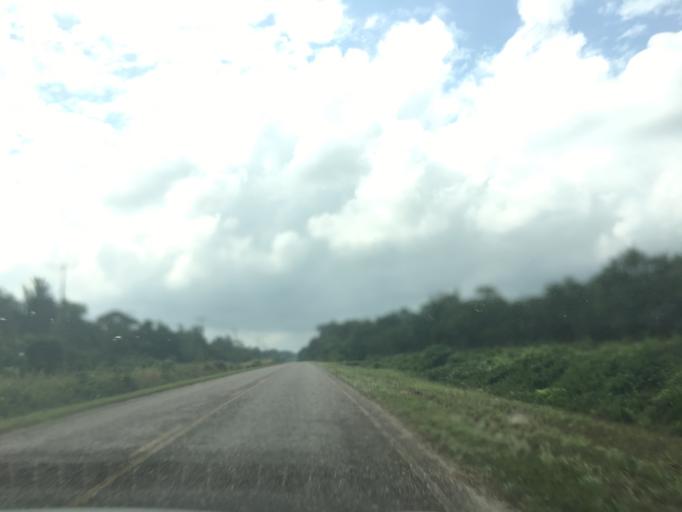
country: BZ
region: Stann Creek
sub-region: Dangriga
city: Dangriga
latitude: 16.9664
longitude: -88.3077
